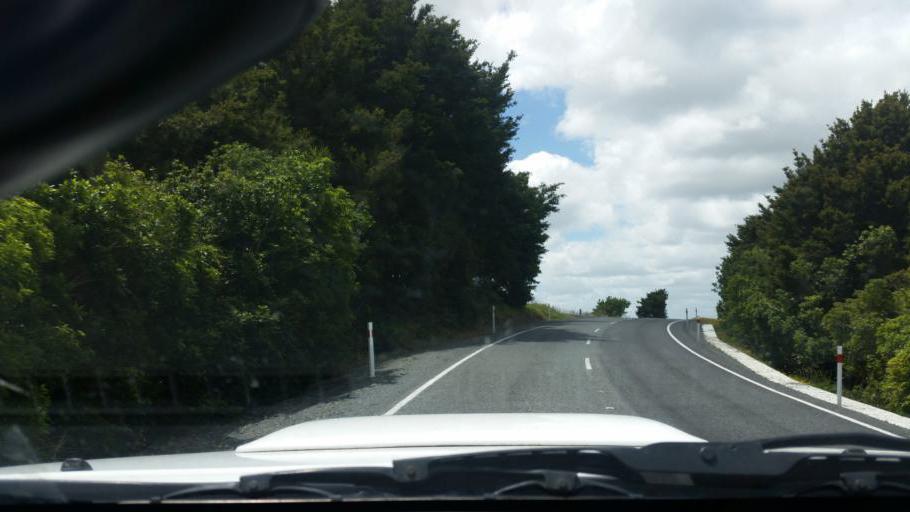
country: NZ
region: Northland
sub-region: Whangarei
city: Ruakaka
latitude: -36.0610
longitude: 174.2718
